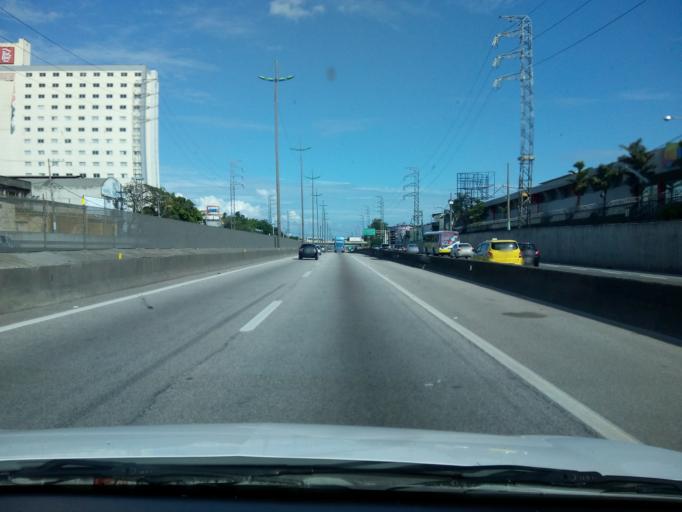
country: BR
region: Rio de Janeiro
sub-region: Sao Joao De Meriti
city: Sao Joao de Meriti
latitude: -22.7917
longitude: -43.3687
